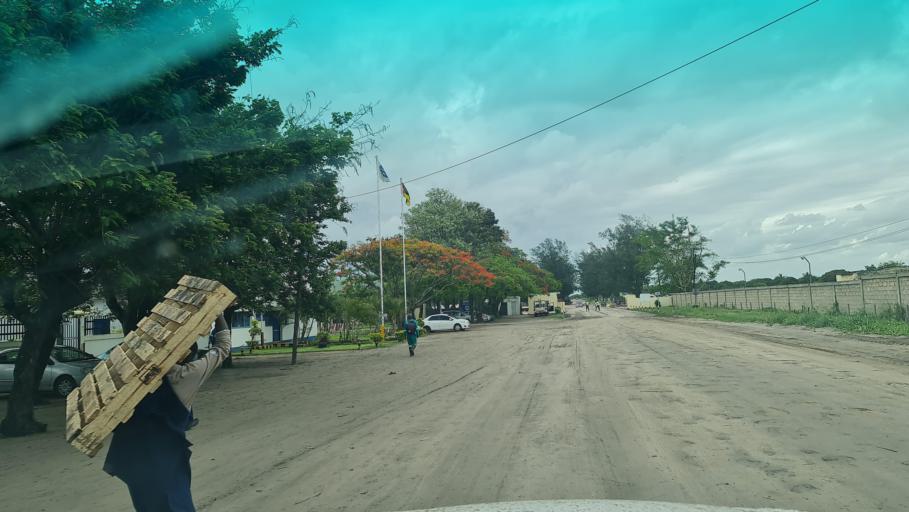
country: MZ
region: Maputo
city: Manhica
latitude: -25.4495
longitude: 32.7774
